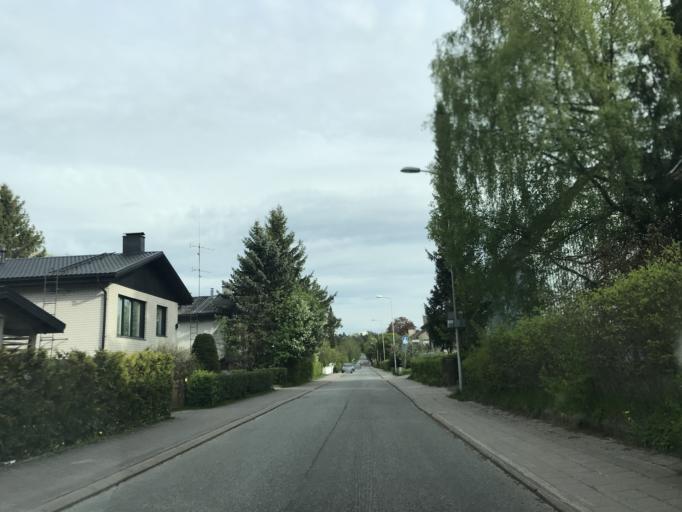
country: FI
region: Varsinais-Suomi
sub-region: Turku
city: Turku
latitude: 60.4415
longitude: 22.2958
